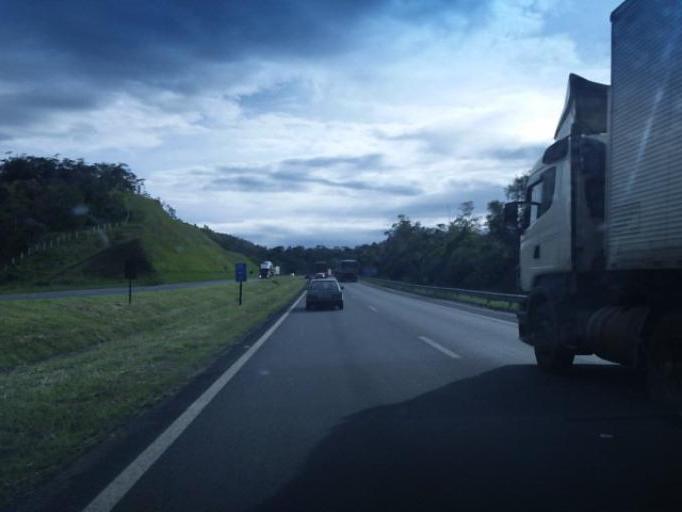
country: BR
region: Parana
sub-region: Antonina
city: Antonina
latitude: -25.1045
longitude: -48.7387
